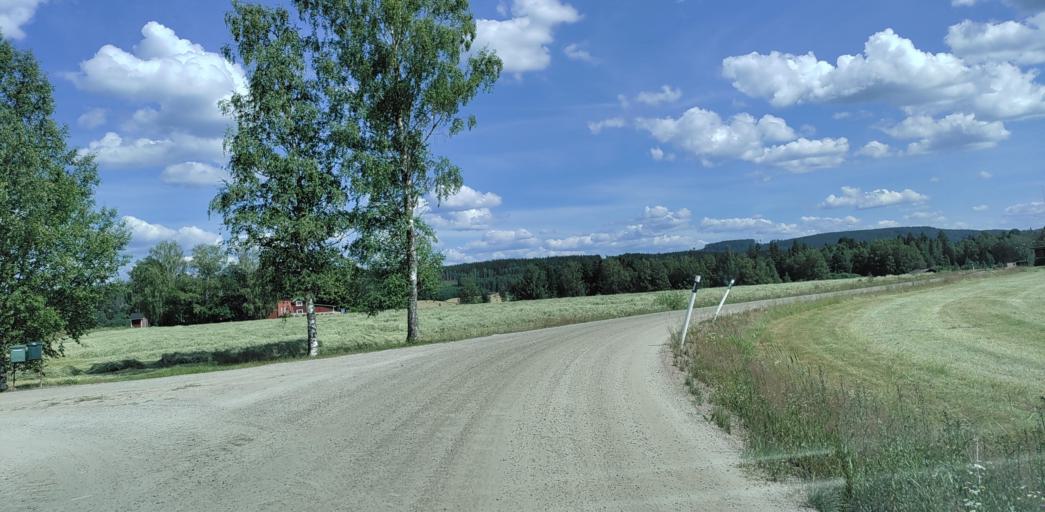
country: SE
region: Vaermland
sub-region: Hagfors Kommun
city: Ekshaerad
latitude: 60.1306
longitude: 13.4642
